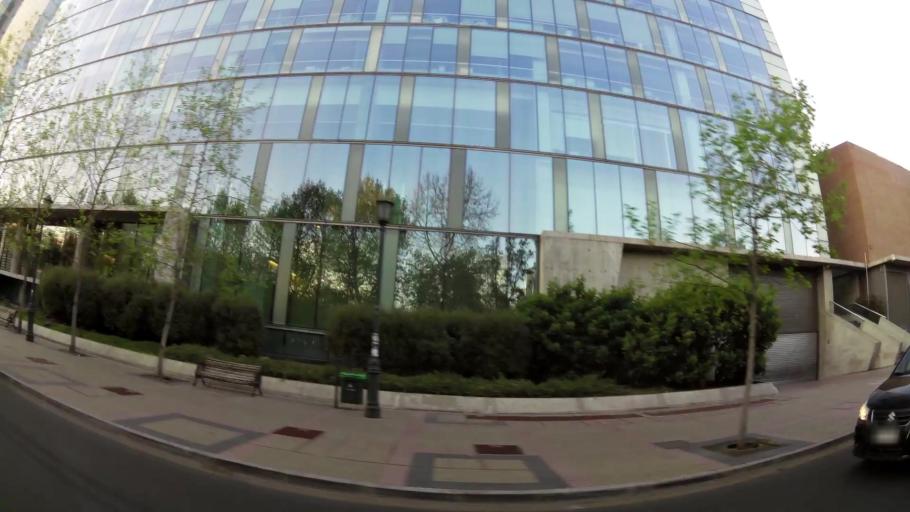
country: CL
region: Santiago Metropolitan
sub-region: Provincia de Santiago
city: Villa Presidente Frei, Nunoa, Santiago, Chile
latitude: -33.4027
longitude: -70.5771
